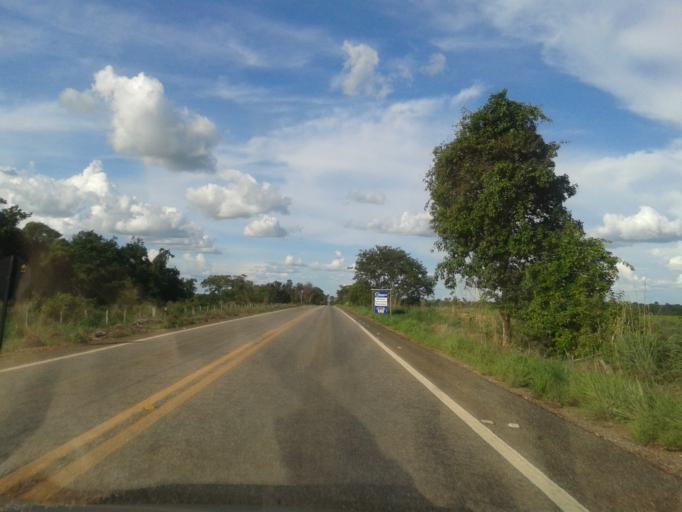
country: BR
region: Goias
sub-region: Mozarlandia
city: Mozarlandia
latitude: -14.5524
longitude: -50.4940
